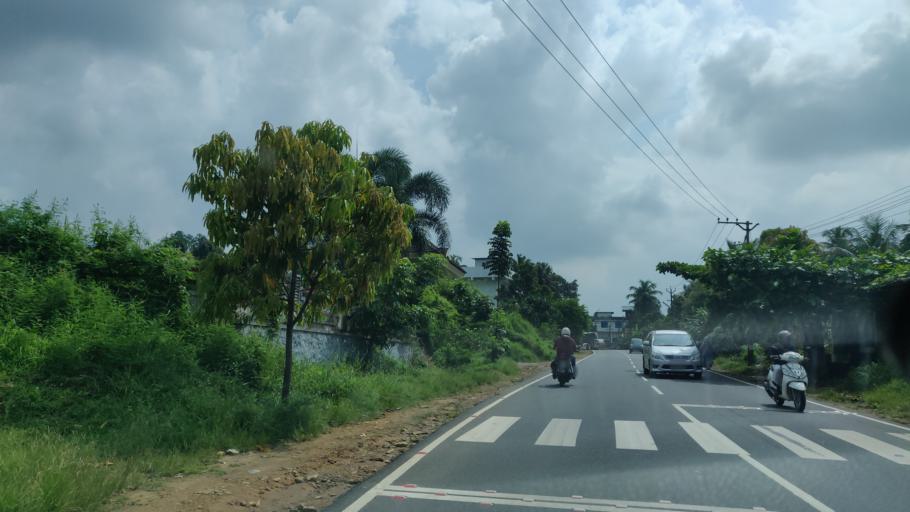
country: IN
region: Kerala
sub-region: Ernakulam
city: Angamali
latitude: 10.1691
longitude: 76.4226
